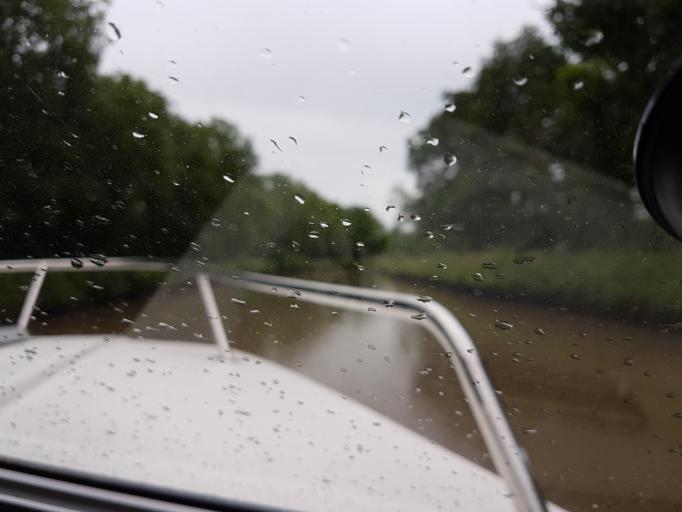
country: FR
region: Bourgogne
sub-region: Departement de la Nievre
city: Corbigny
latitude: 47.3654
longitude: 3.6144
